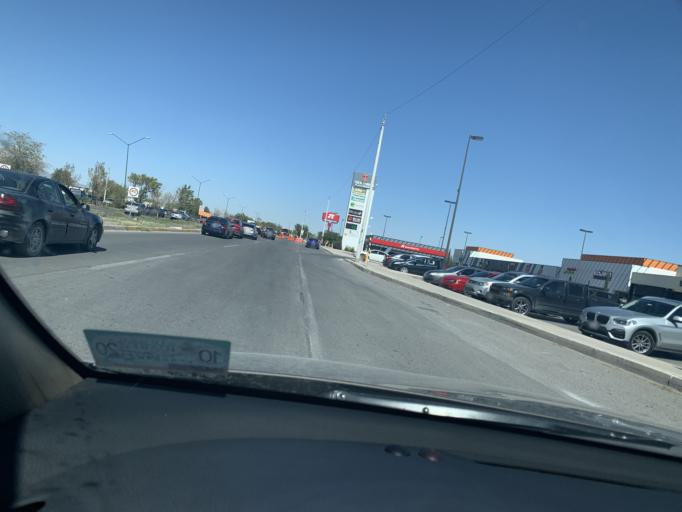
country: US
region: Texas
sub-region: El Paso County
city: Socorro
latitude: 31.7008
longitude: -106.3826
